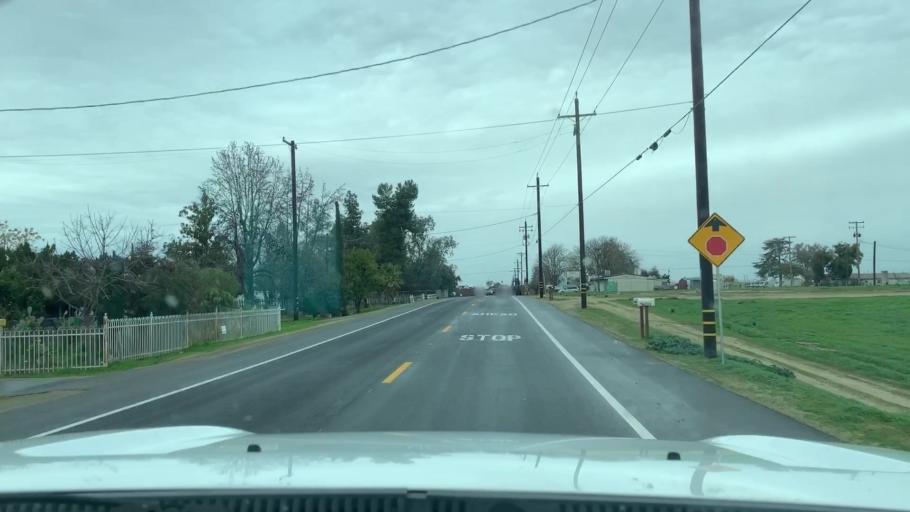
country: US
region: California
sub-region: Fresno County
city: Fowler
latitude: 36.5747
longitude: -119.6825
